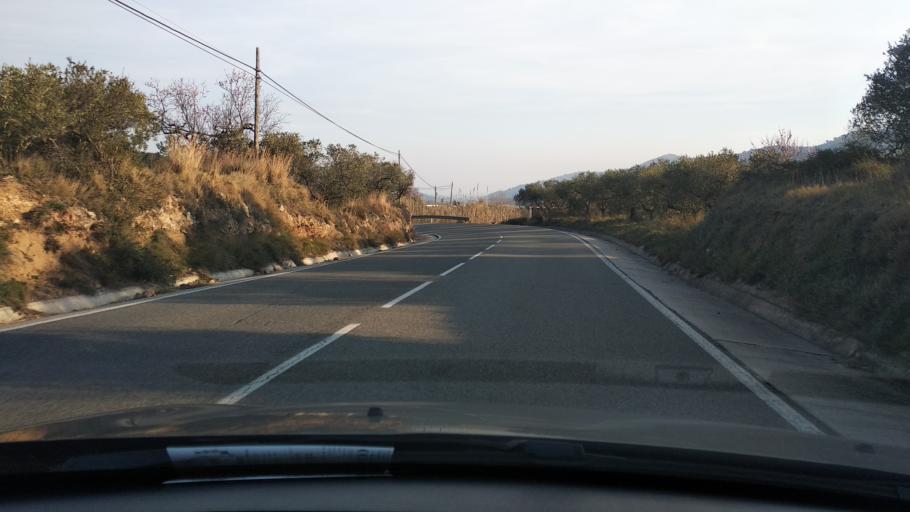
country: ES
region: Catalonia
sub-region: Provincia de Tarragona
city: Alforja
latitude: 41.2172
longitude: 0.9715
